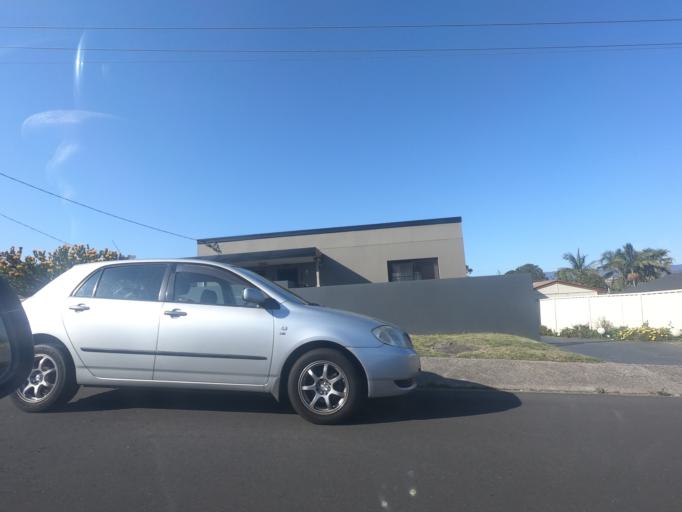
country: AU
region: New South Wales
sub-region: Wollongong
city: Koonawarra
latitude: -34.4901
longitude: 150.8006
